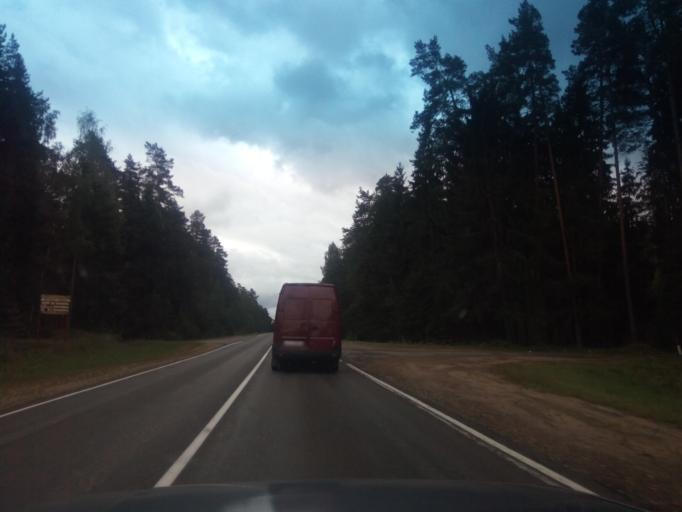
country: BY
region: Vitebsk
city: Polatsk
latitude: 55.4014
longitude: 28.8080
